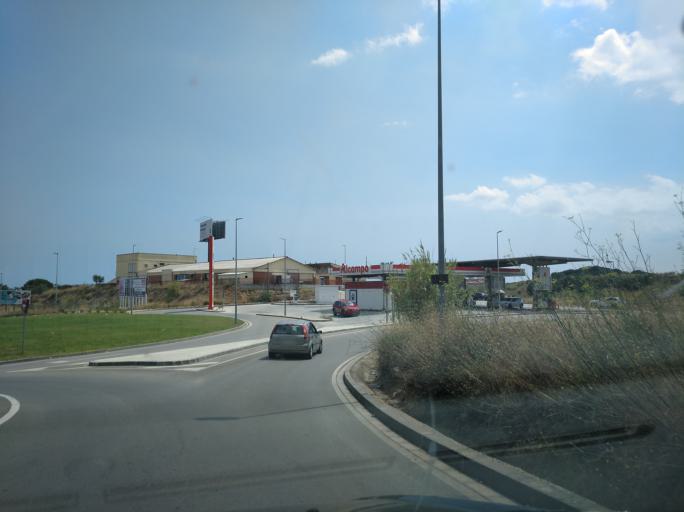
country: ES
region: Catalonia
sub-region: Provincia de Barcelona
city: Mataro
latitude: 41.5539
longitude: 2.4301
